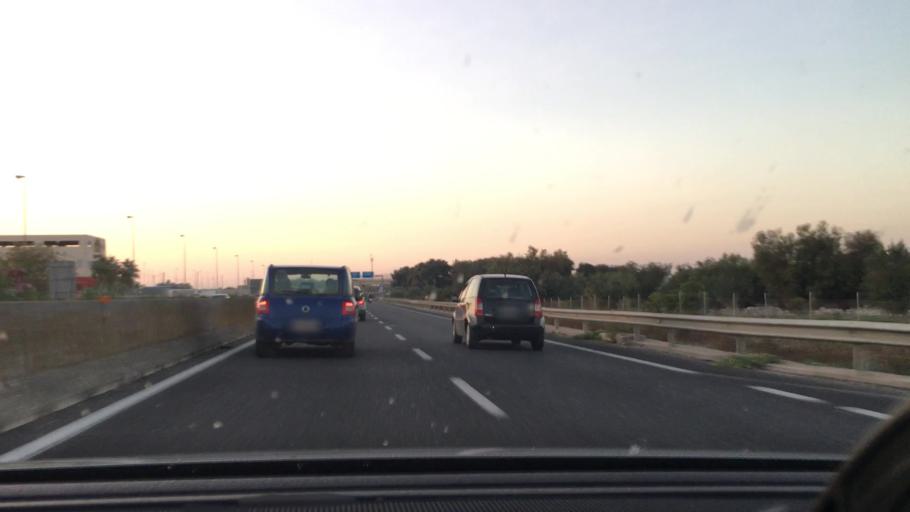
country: IT
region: Apulia
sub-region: Provincia di Lecce
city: Surbo
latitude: 40.3971
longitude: 18.1154
